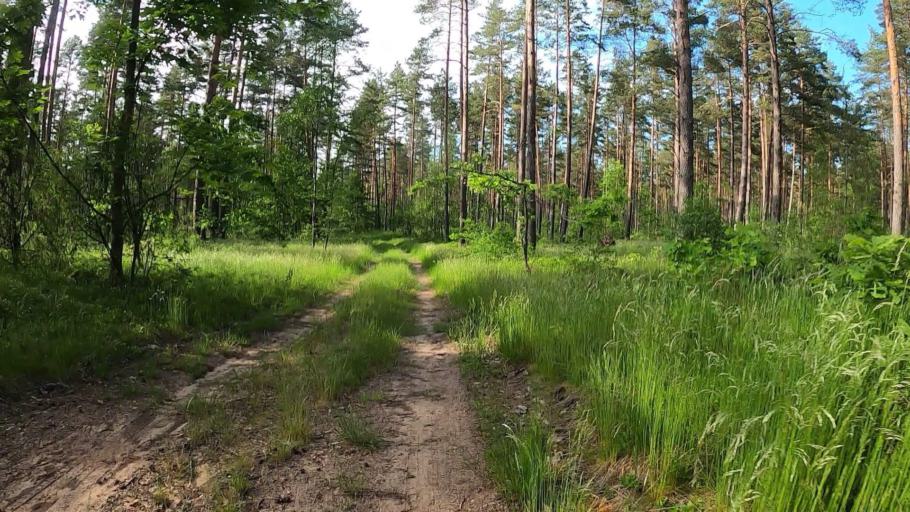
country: LV
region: Riga
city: Bergi
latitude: 57.0145
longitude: 24.2431
